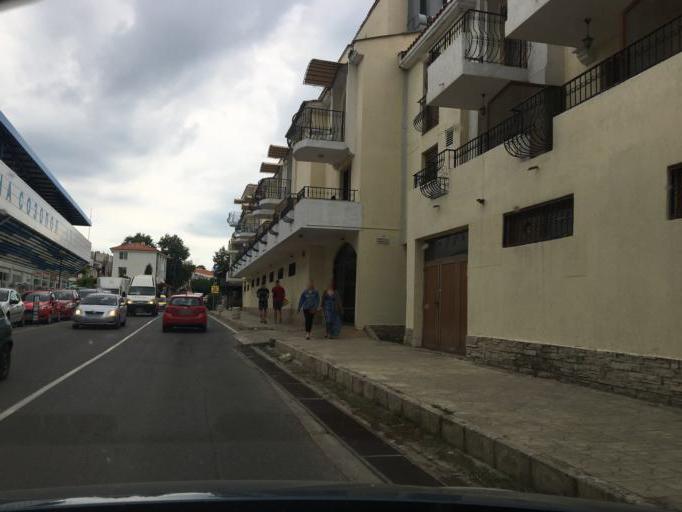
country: BG
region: Burgas
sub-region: Obshtina Sozopol
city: Sozopol
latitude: 42.4134
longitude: 27.6977
